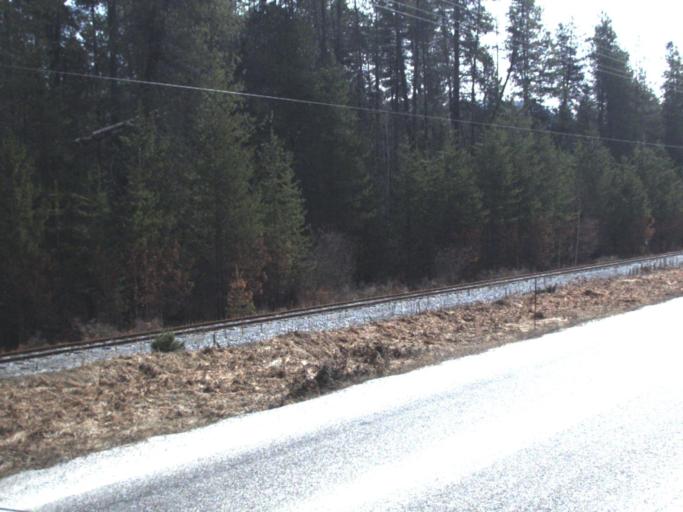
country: CA
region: British Columbia
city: Fruitvale
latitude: 48.6576
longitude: -117.3880
